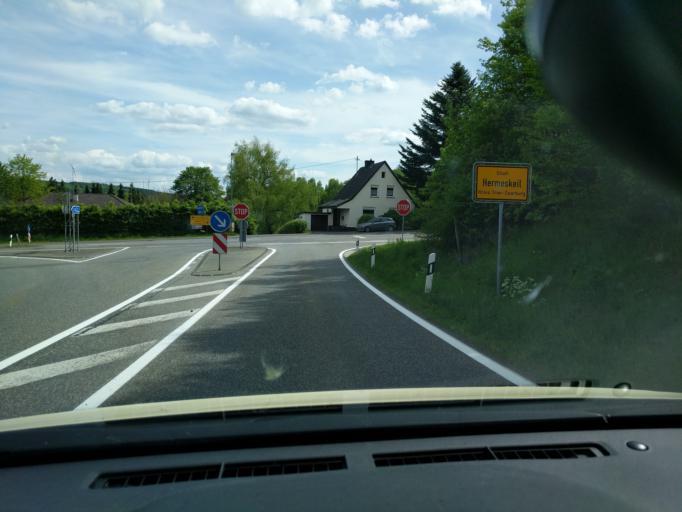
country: DE
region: Rheinland-Pfalz
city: Hermeskeil
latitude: 49.6586
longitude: 6.9247
